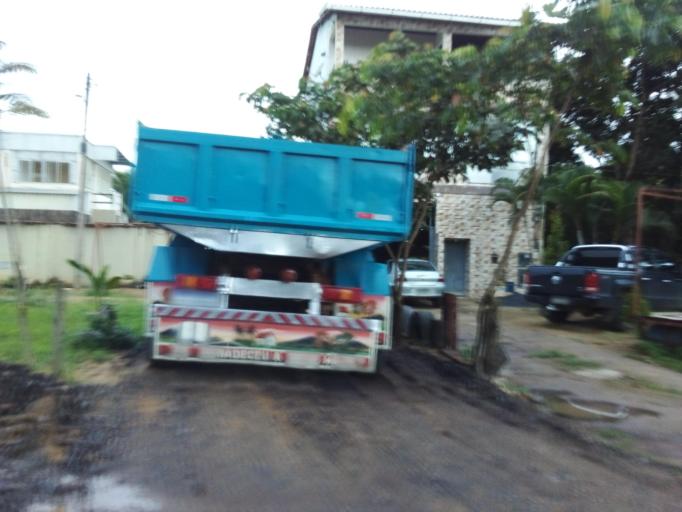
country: BR
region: Espirito Santo
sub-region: Marilandia
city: Marilandia
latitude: -19.5327
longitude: -40.4889
